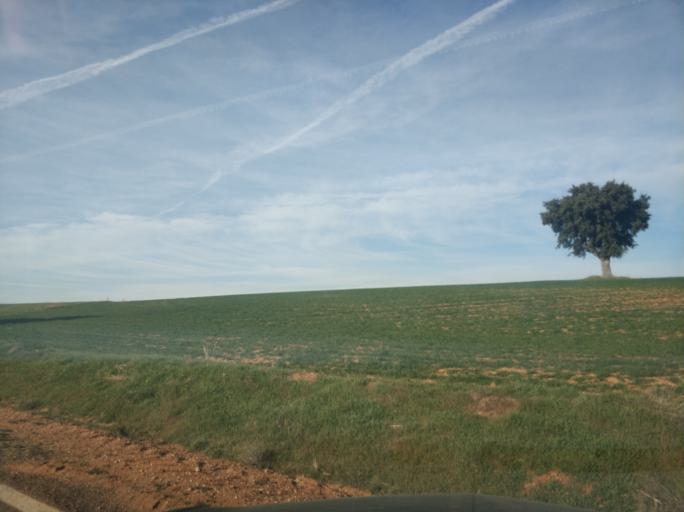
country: ES
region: Castille and Leon
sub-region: Provincia de Salamanca
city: Parada de Arriba
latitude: 41.0013
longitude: -5.8127
